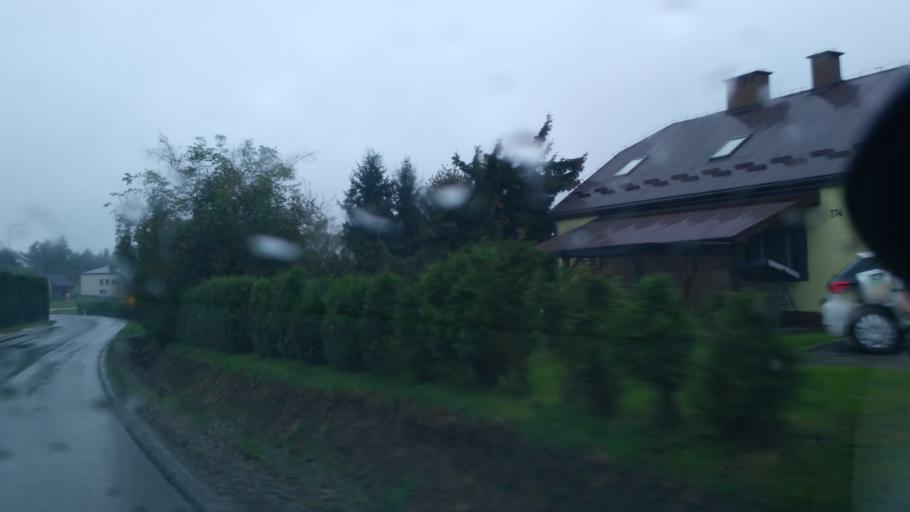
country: PL
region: Subcarpathian Voivodeship
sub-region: Powiat krosnienski
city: Korczyna
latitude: 49.7033
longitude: 21.8124
